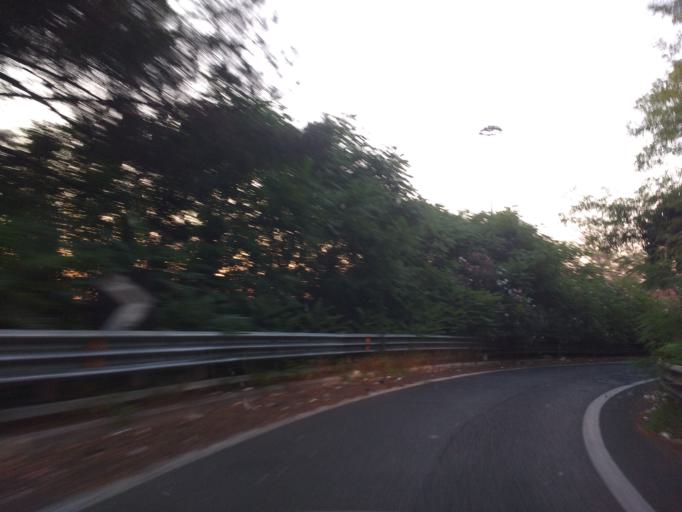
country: IT
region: Latium
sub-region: Citta metropolitana di Roma Capitale
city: Vitinia
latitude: 41.8079
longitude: 12.4211
